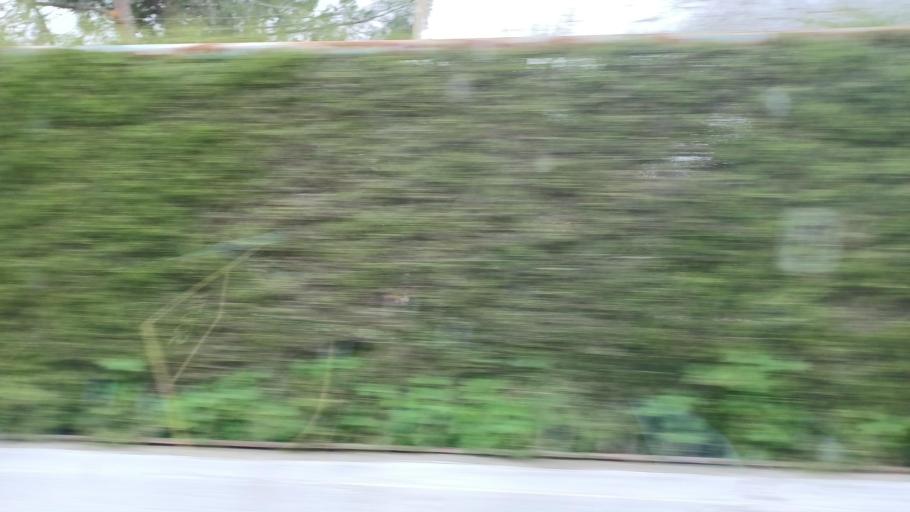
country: CY
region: Limassol
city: Pyrgos
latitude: 34.7771
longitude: 33.2538
